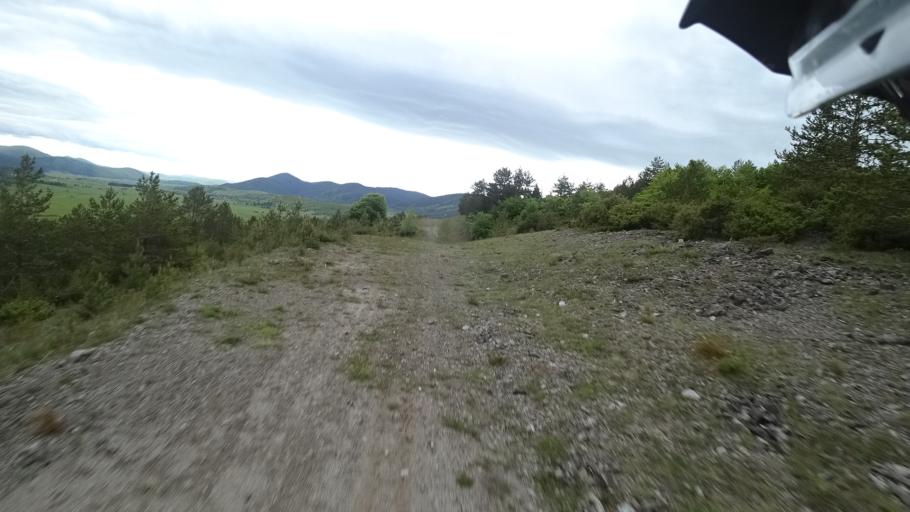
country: HR
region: Licko-Senjska
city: Jezerce
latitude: 44.8674
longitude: 15.4426
